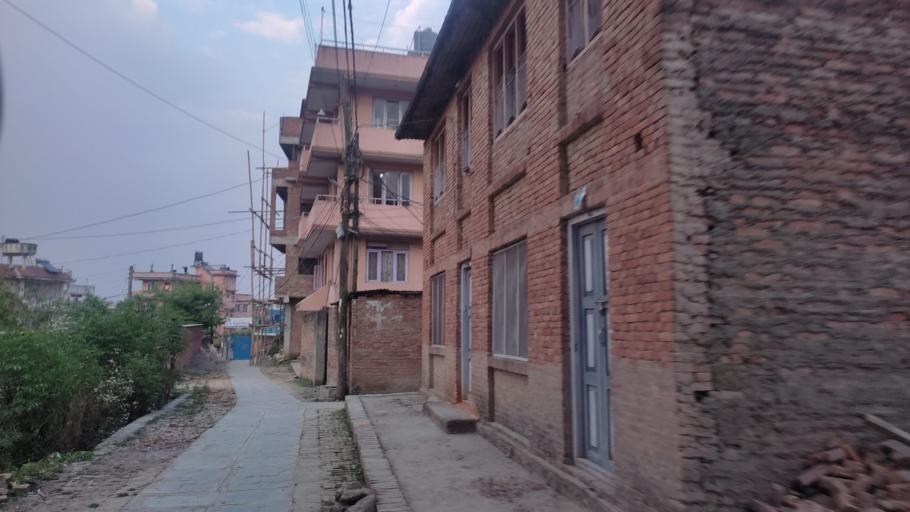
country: NP
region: Central Region
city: Kirtipur
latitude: 27.6719
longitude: 85.2803
